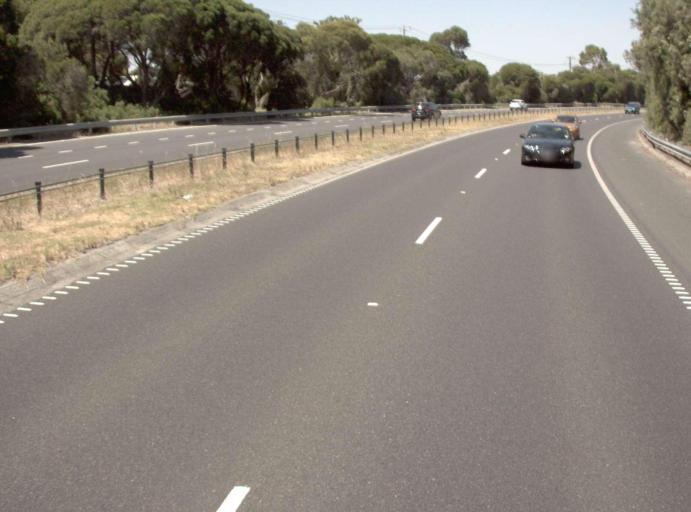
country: AU
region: Victoria
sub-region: Frankston
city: Frankston East
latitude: -38.1327
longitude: 145.1360
